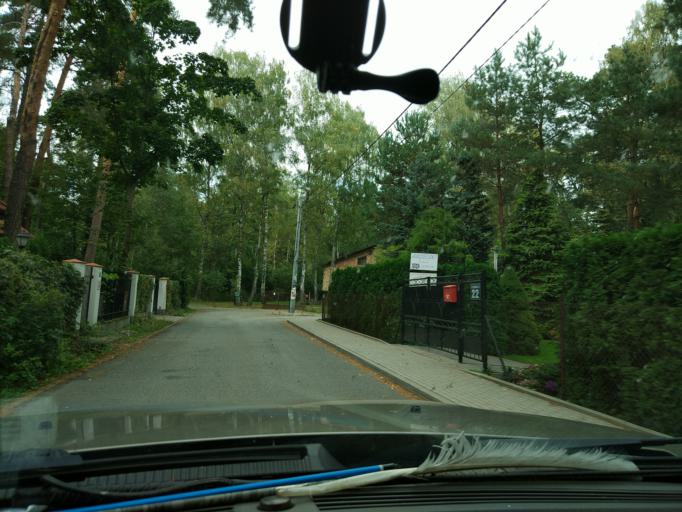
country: PL
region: Masovian Voivodeship
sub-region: Powiat grodziski
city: Podkowa Lesna
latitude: 52.1264
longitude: 20.7410
